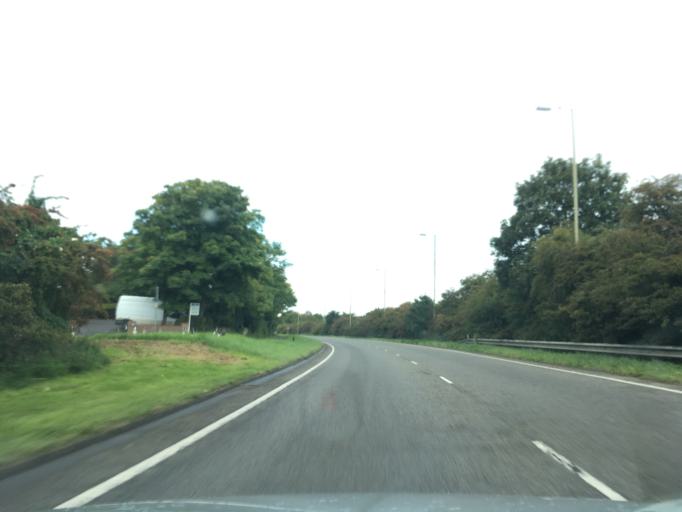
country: GB
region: England
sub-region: Oxfordshire
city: Cowley
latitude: 51.7649
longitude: -1.1993
